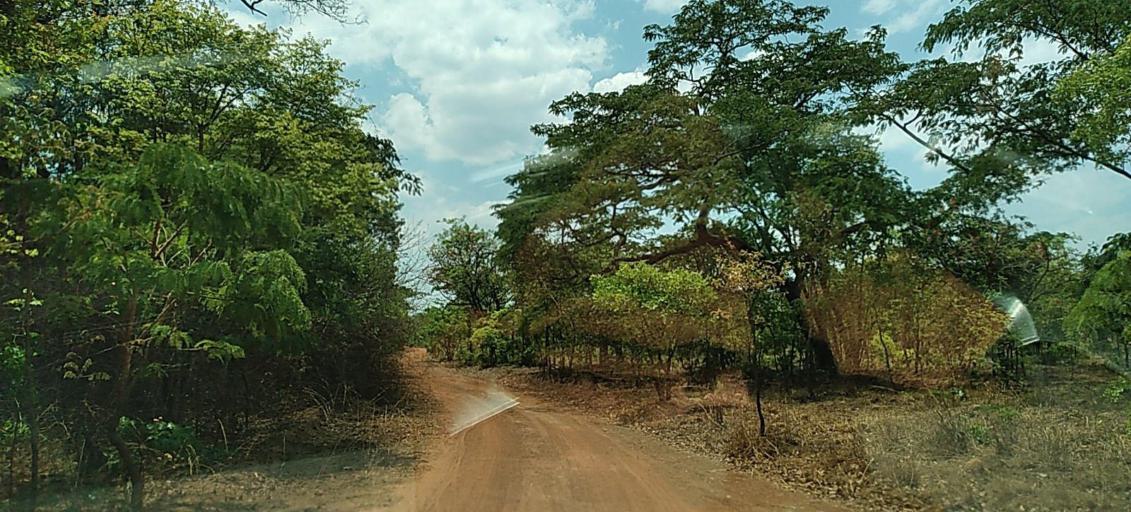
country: ZM
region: Copperbelt
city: Chililabombwe
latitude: -12.5277
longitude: 27.6277
